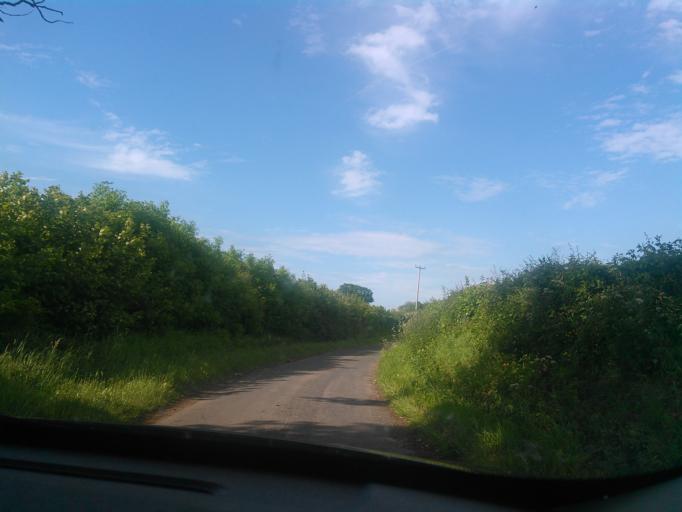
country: GB
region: England
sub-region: Shropshire
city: Stoke upon Tern
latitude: 52.7905
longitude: -2.5668
